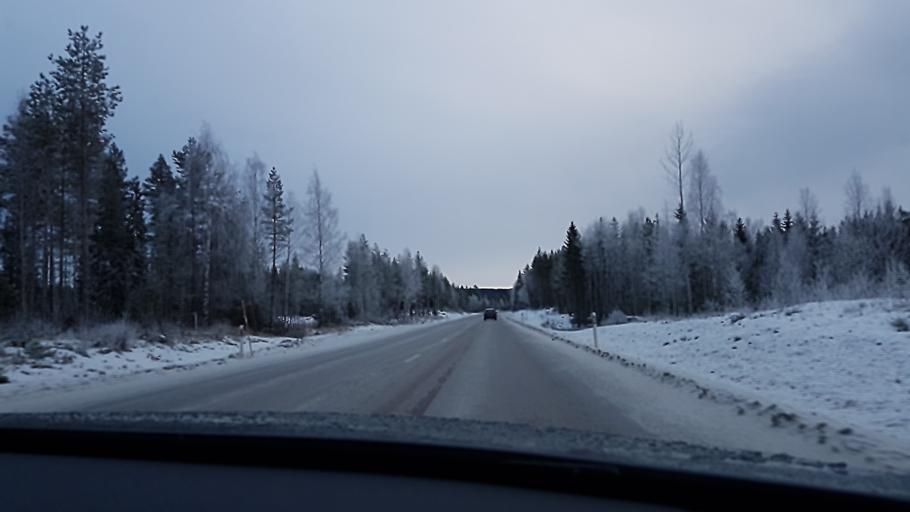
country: SE
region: Jaemtland
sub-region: Bergs Kommun
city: Hoverberg
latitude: 62.8146
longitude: 14.5172
